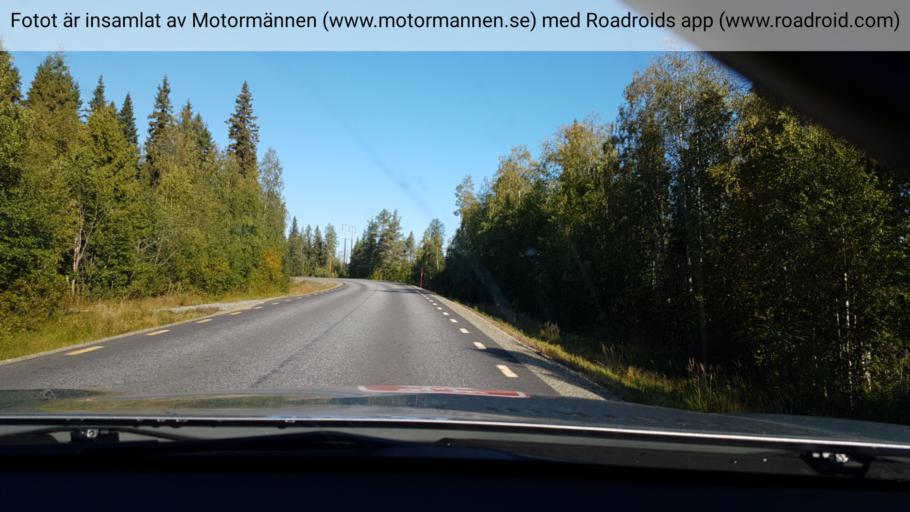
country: SE
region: Vaesterbotten
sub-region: Vindelns Kommun
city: Vindeln
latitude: 64.4167
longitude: 19.3649
